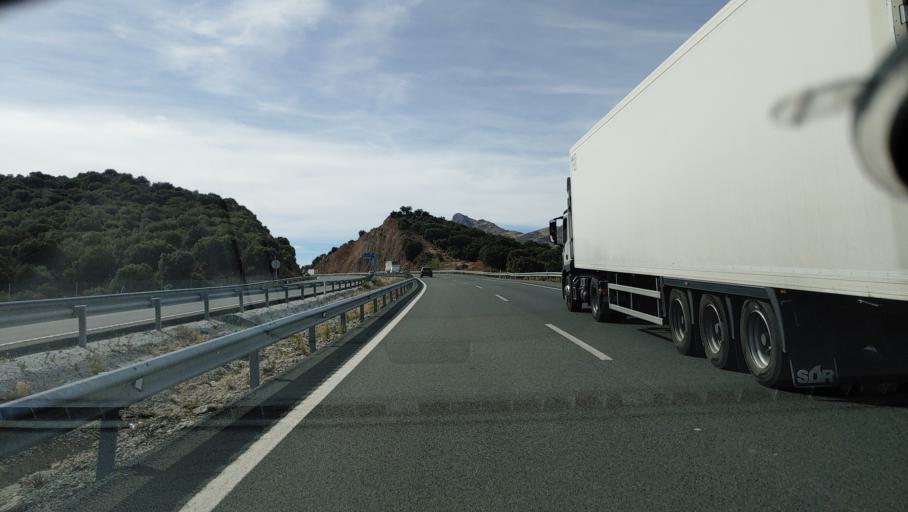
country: ES
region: Andalusia
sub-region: Provincia de Granada
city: Beas de Granada
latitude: 37.2993
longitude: -3.4395
